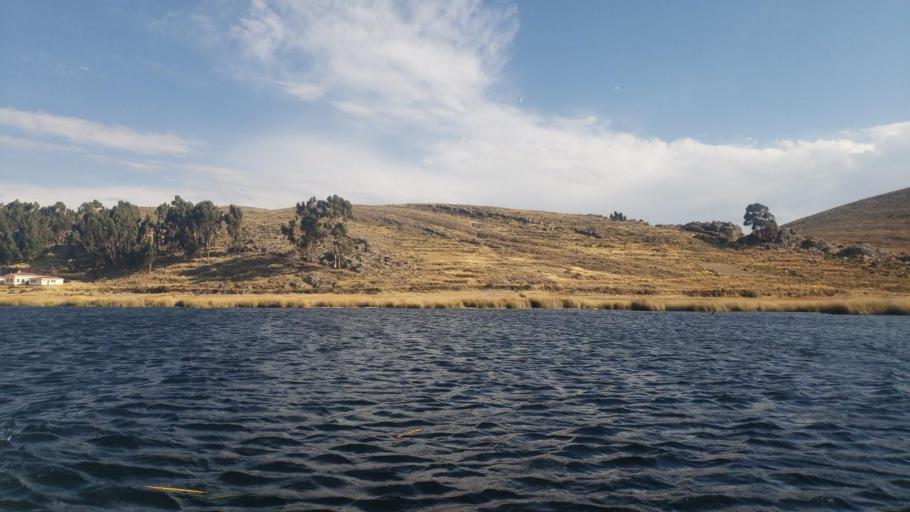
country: BO
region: La Paz
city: Huatajata
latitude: -16.3301
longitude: -68.7183
